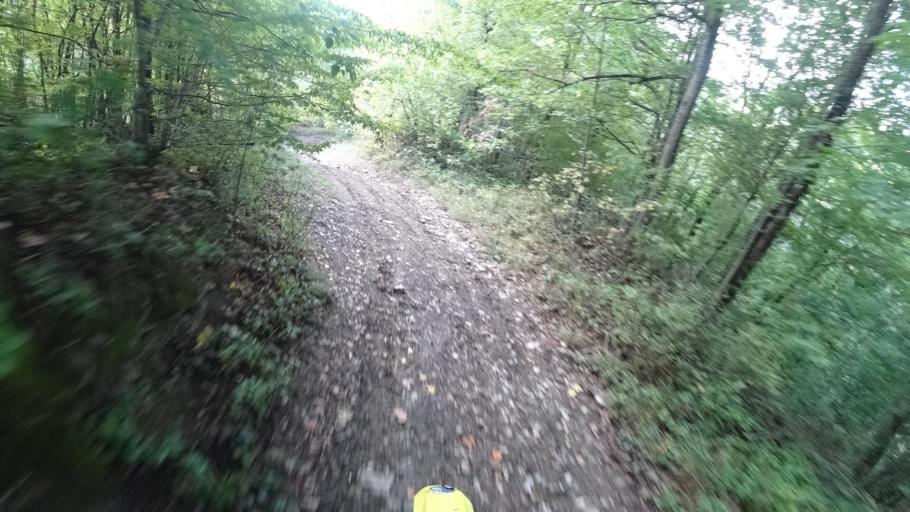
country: BA
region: Republika Srpska
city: Hiseti
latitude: 44.7600
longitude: 17.1577
